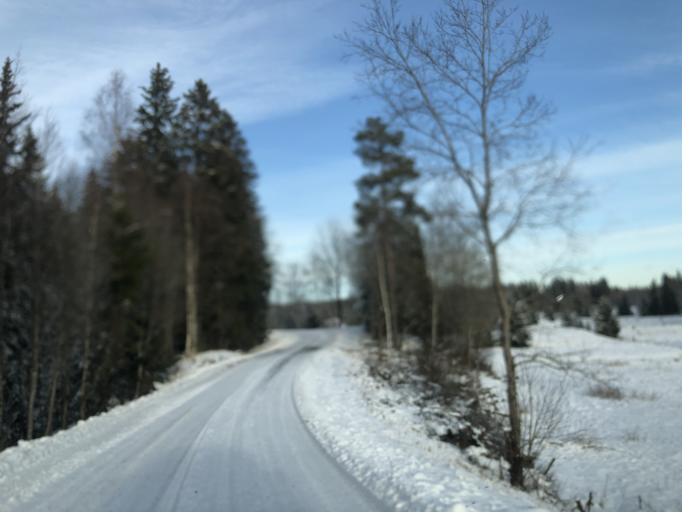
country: SE
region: Vaestra Goetaland
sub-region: Ulricehamns Kommun
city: Ulricehamn
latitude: 57.7654
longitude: 13.5197
